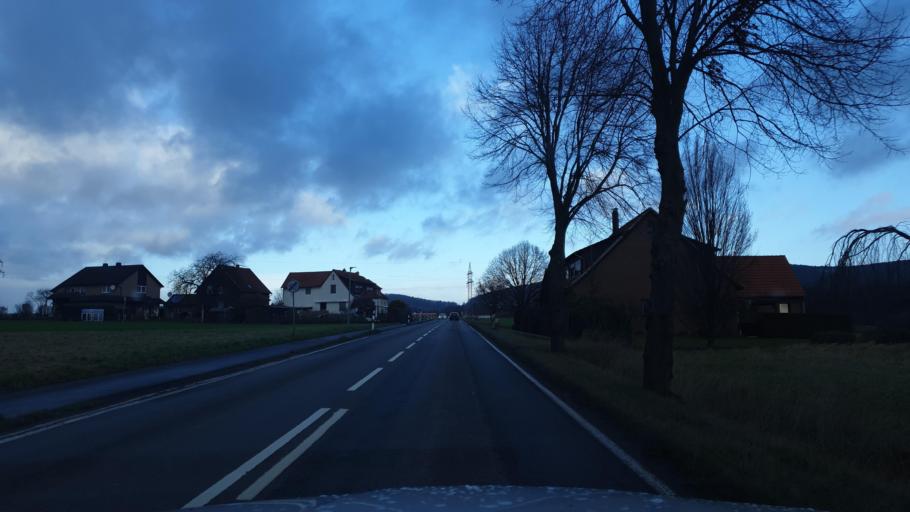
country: DE
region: North Rhine-Westphalia
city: Bad Oeynhausen
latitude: 52.2416
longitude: 8.7862
